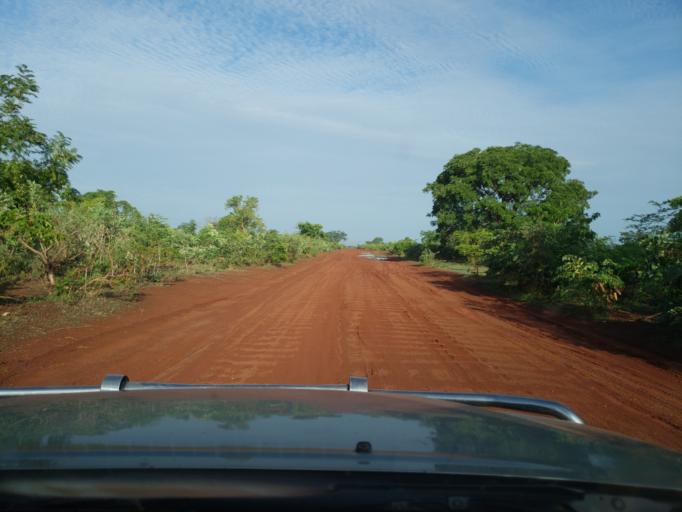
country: ML
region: Sikasso
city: Koutiala
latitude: 12.4267
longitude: -5.6387
